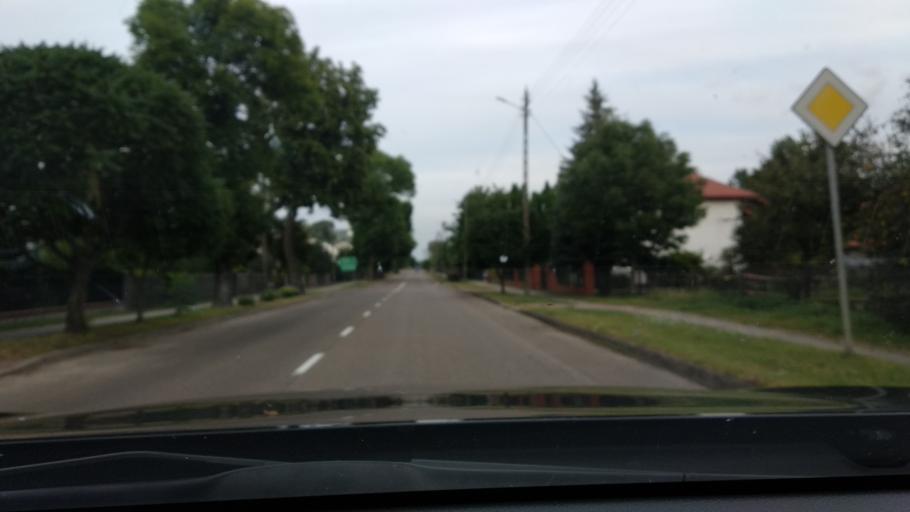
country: PL
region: Masovian Voivodeship
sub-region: Powiat pultuski
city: Obryte
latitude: 52.7162
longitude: 21.2486
